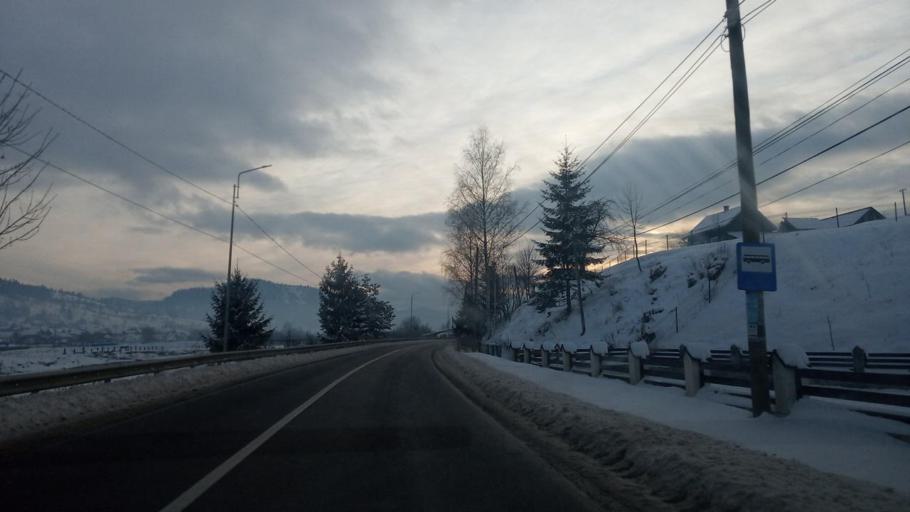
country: RO
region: Suceava
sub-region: Comuna Frasin
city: Frasin
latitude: 47.5084
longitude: 25.7973
